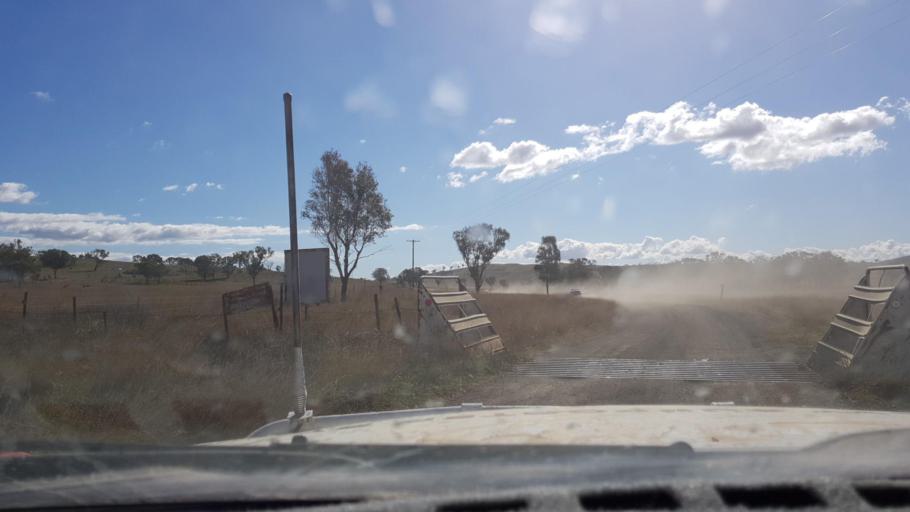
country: AU
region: New South Wales
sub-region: Narrabri
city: Blair Athol
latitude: -30.5024
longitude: 150.4398
